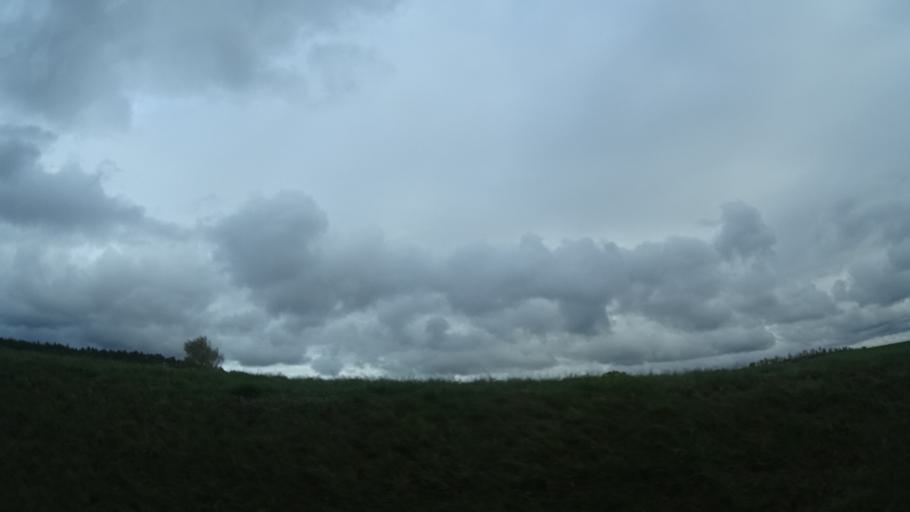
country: DE
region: Bavaria
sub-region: Regierungsbezirk Unterfranken
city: Hohenroth
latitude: 50.3429
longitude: 10.1386
